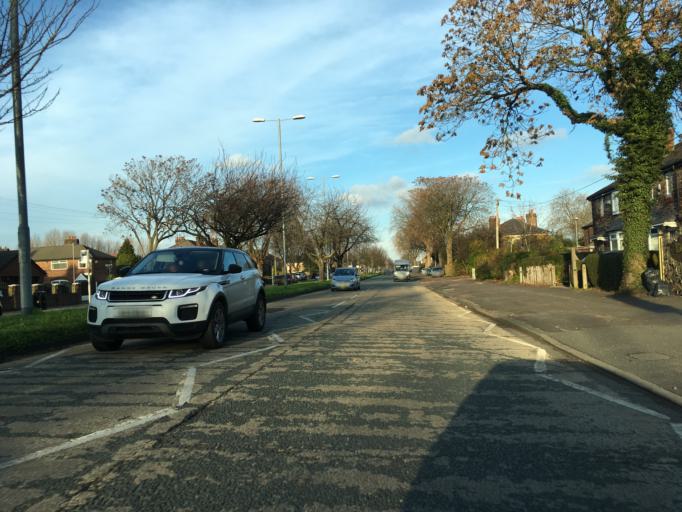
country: GB
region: England
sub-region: Manchester
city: Burnage
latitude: 53.4296
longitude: -2.2092
